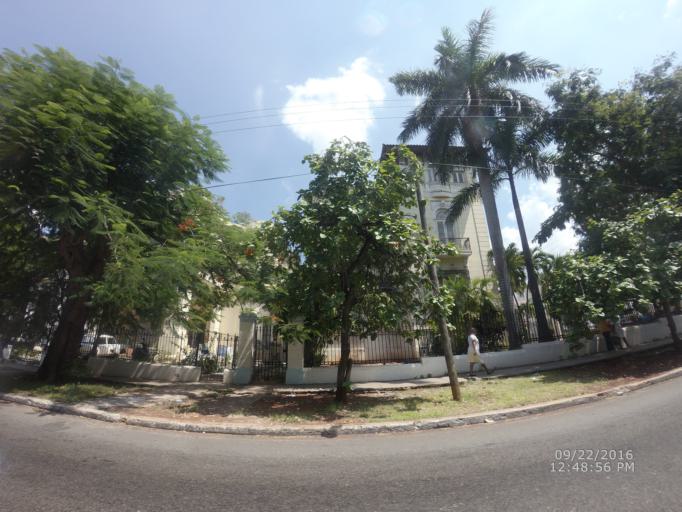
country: CU
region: La Habana
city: Havana
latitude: 23.1335
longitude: -82.3960
